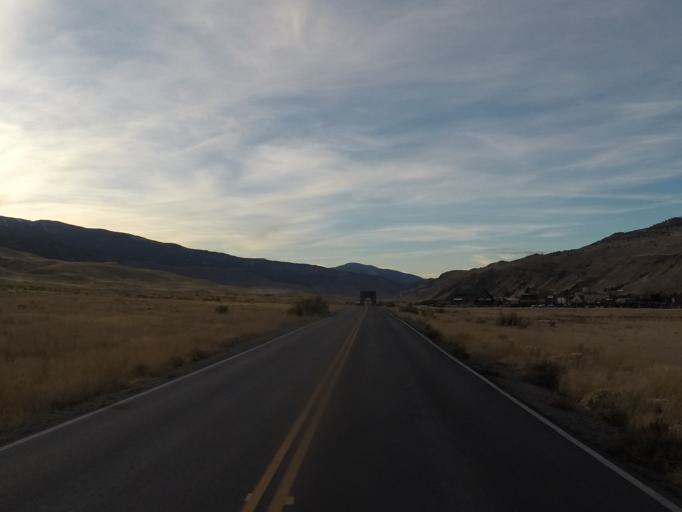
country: US
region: Montana
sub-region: Gallatin County
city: West Yellowstone
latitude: 45.0268
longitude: -110.7036
